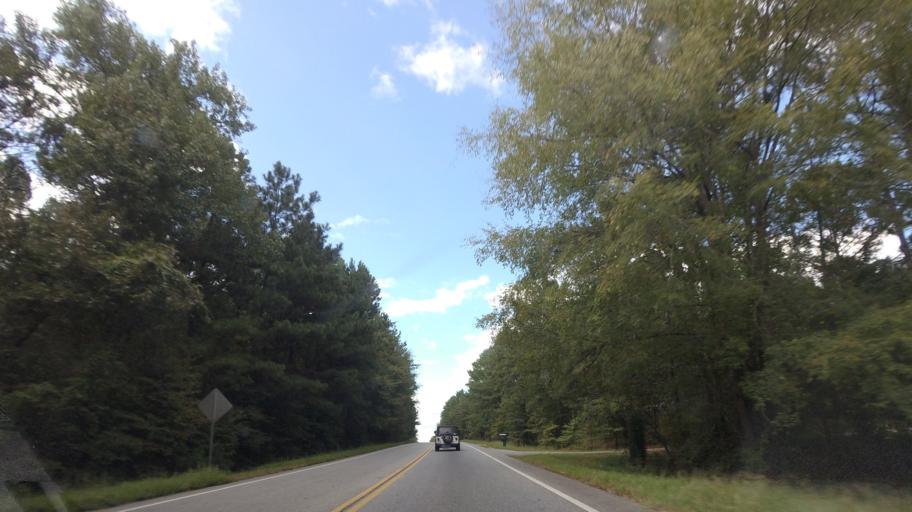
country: US
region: Georgia
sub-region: Bibb County
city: Macon
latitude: 32.9652
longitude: -83.7263
